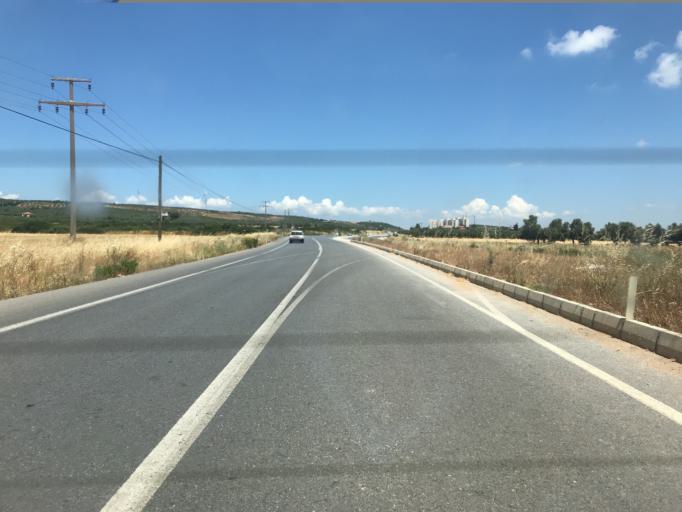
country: TR
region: Aydin
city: Akkoy
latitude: 37.4633
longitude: 27.3390
